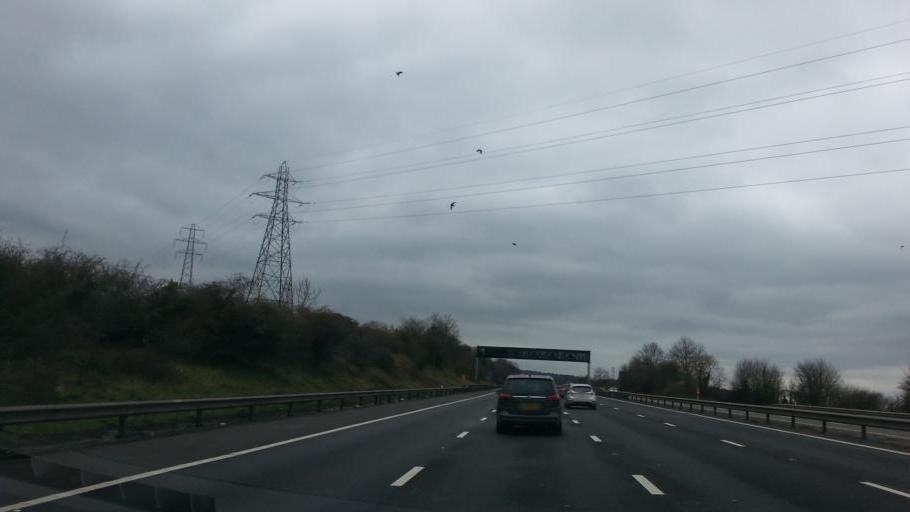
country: GB
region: England
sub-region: North Somerset
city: Portishead
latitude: 51.4696
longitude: -2.7391
